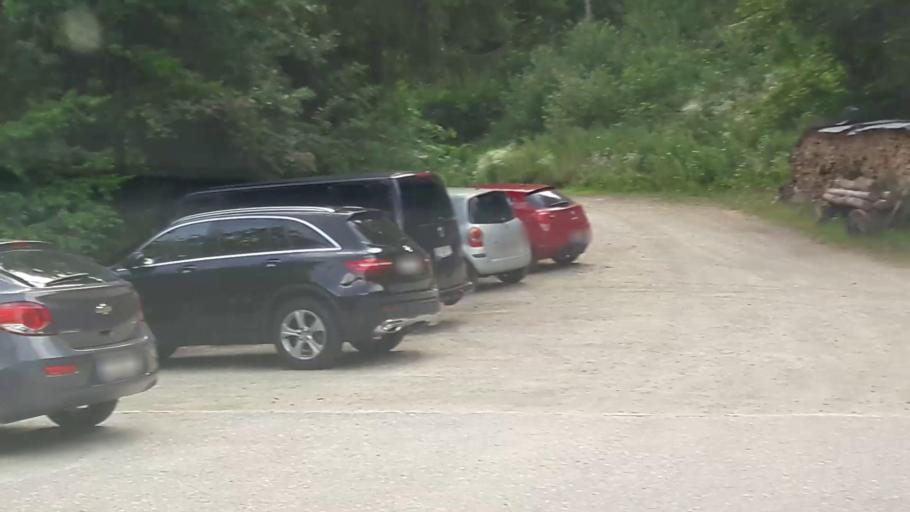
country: AT
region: Upper Austria
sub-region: Politischer Bezirk Rohrbach
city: Atzesberg
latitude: 48.4756
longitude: 13.9248
